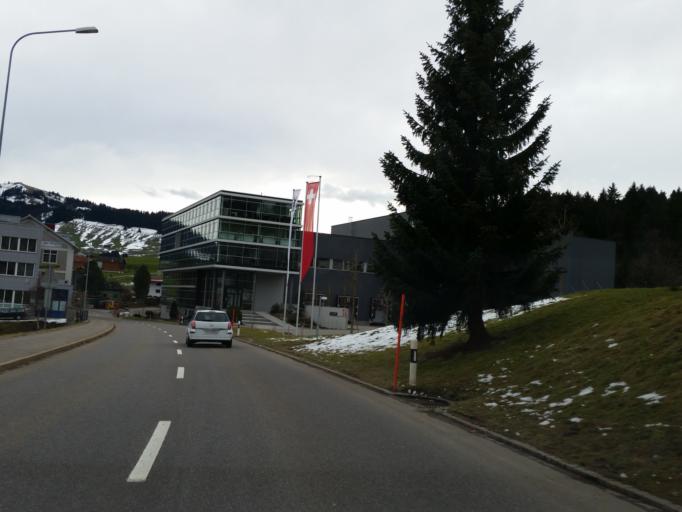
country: CH
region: Appenzell Ausserrhoden
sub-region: Bezirk Hinterland
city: Waldstatt
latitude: 47.3542
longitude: 9.2835
